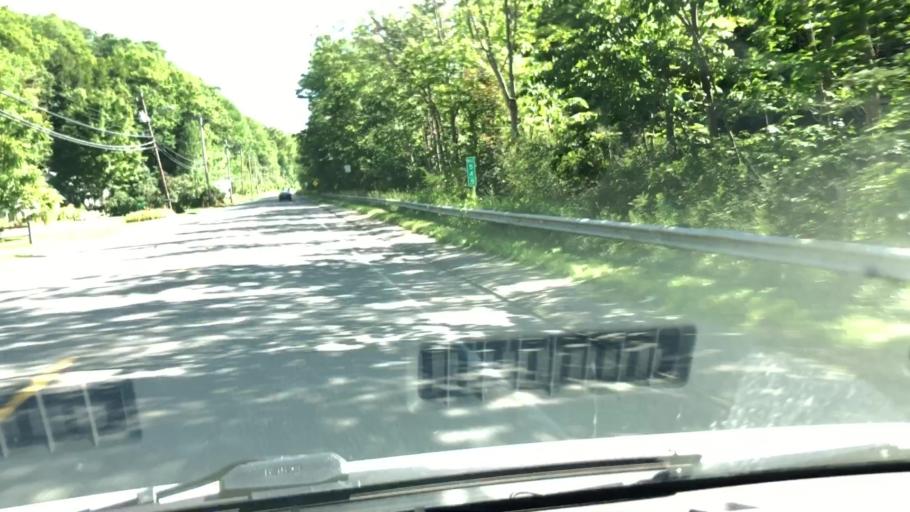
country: US
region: Massachusetts
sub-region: Berkshire County
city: Adams
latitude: 42.5991
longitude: -73.1392
